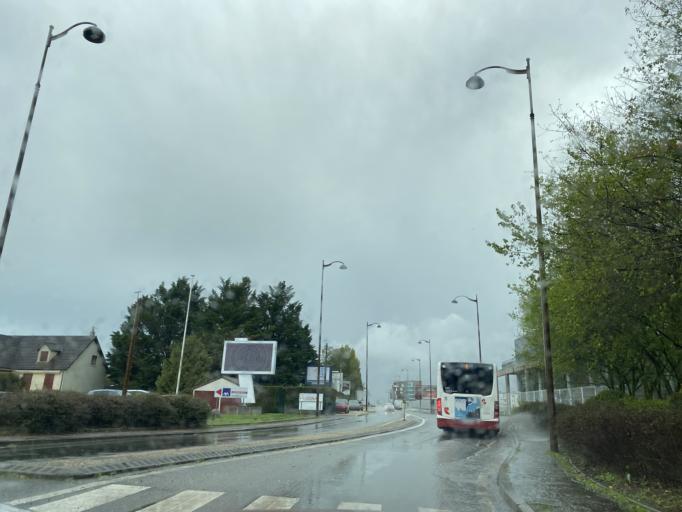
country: FR
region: Centre
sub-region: Departement du Cher
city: Bourges
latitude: 47.0663
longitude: 2.3712
